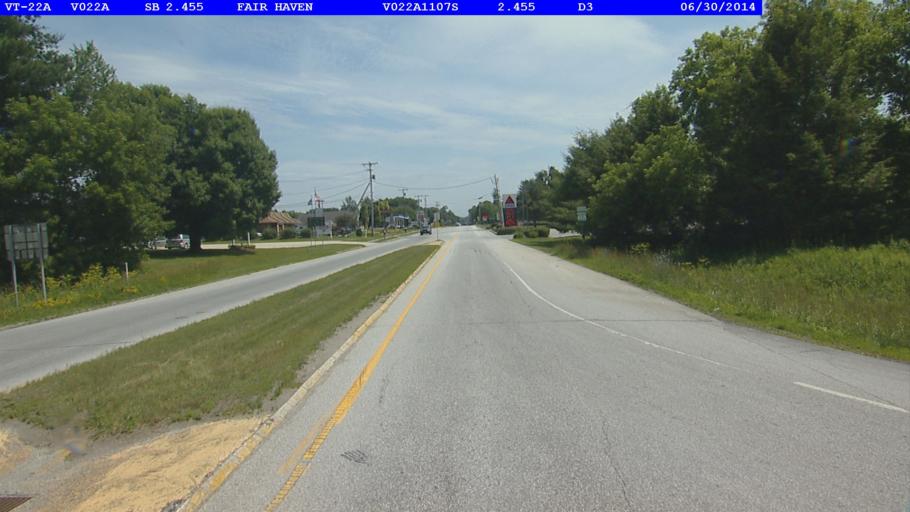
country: US
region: Vermont
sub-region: Rutland County
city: Fair Haven
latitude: 43.6049
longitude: -73.2773
